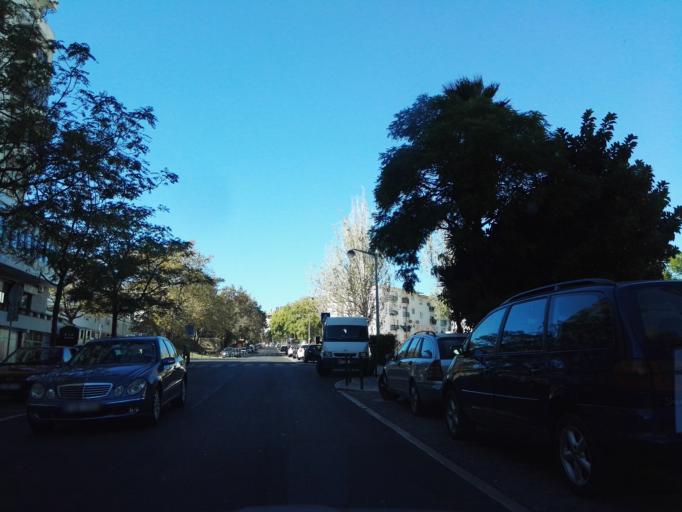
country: PT
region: Lisbon
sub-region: Loures
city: Moscavide
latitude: 38.7755
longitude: -9.1126
